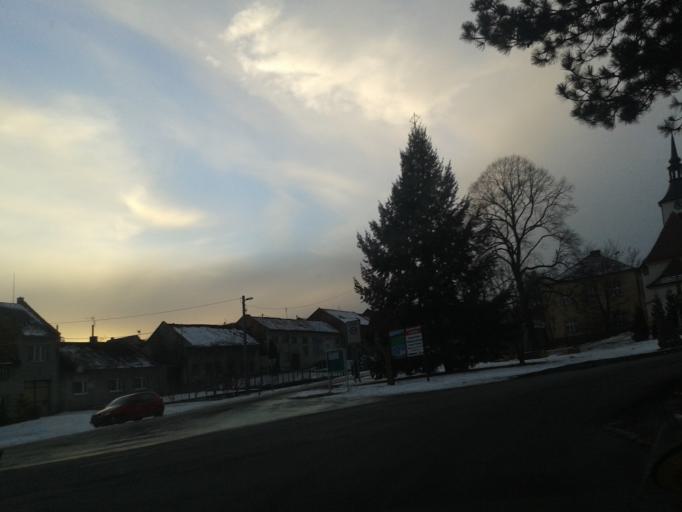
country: CZ
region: Olomoucky
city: Pteni
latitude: 49.4882
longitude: 16.9613
